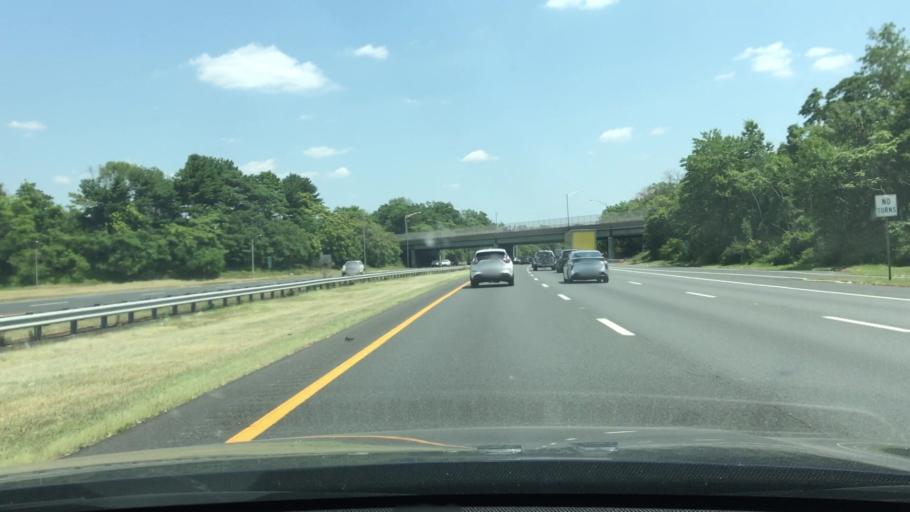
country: US
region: New Jersey
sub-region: Somerset County
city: Finderne
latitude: 40.5693
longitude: -74.5589
